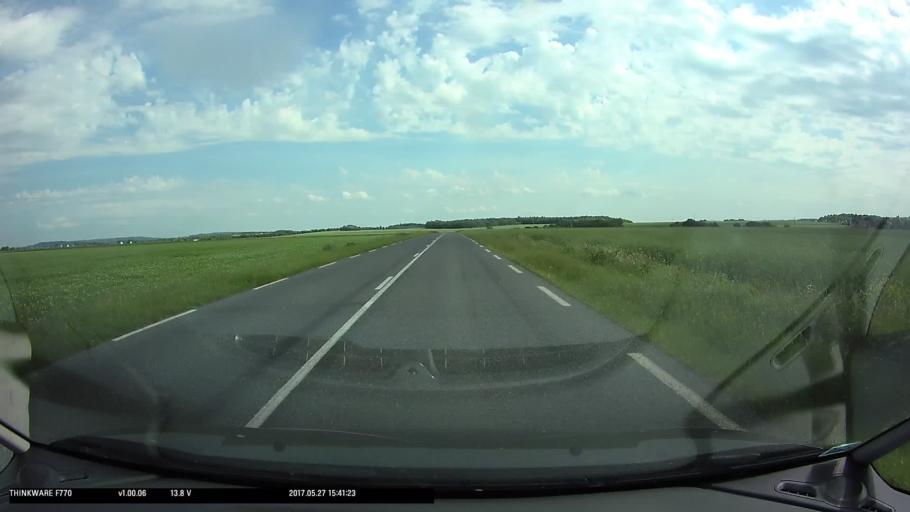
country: FR
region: Picardie
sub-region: Departement de l'Oise
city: Chaumont-en-Vexin
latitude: 49.2311
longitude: 1.8812
